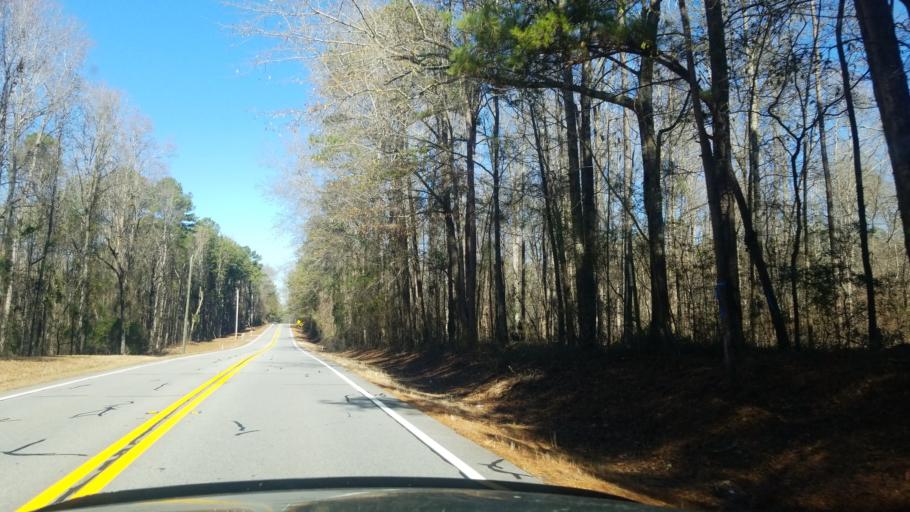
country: US
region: Georgia
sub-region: Harris County
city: Hamilton
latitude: 32.6715
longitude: -84.8589
